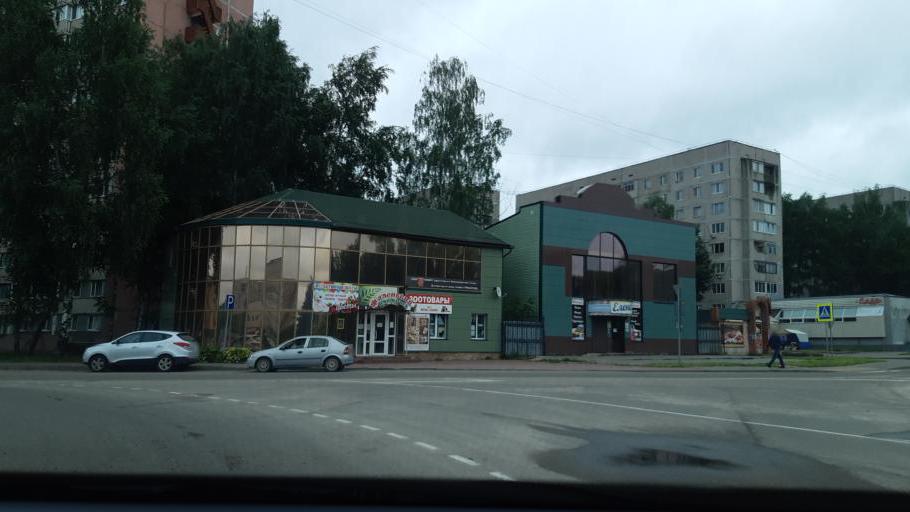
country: RU
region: Smolensk
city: Desnogorsk
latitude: 54.1522
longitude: 33.2882
